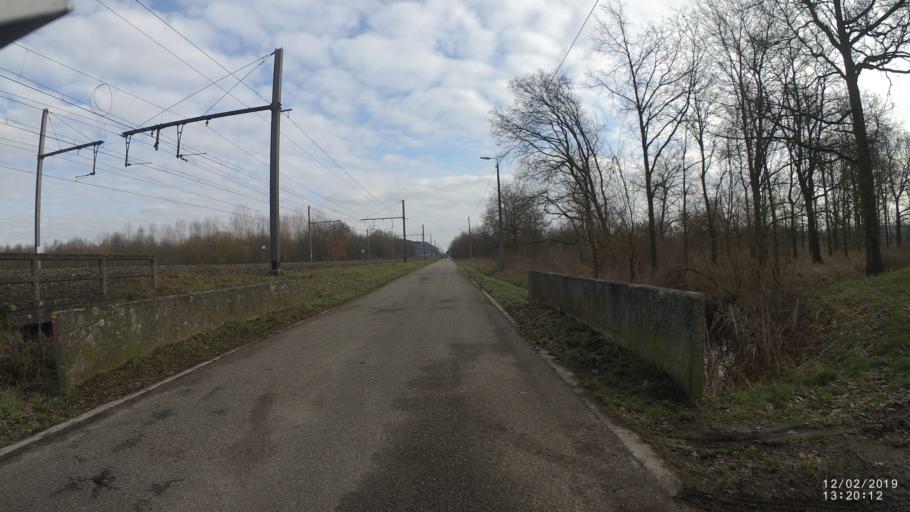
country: BE
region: Flanders
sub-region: Provincie Vlaams-Brabant
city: Scherpenheuvel-Zichem
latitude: 51.0100
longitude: 4.9388
